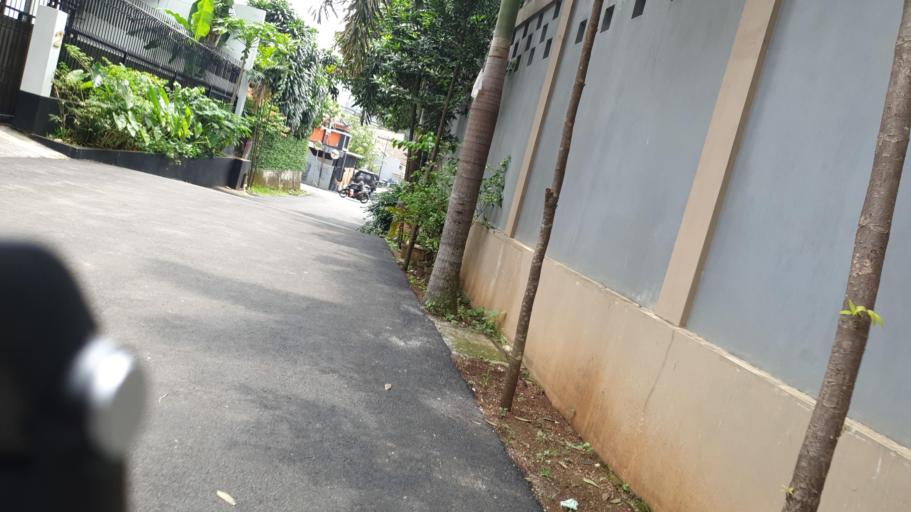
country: ID
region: Jakarta Raya
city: Jakarta
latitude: -6.2729
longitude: 106.7944
